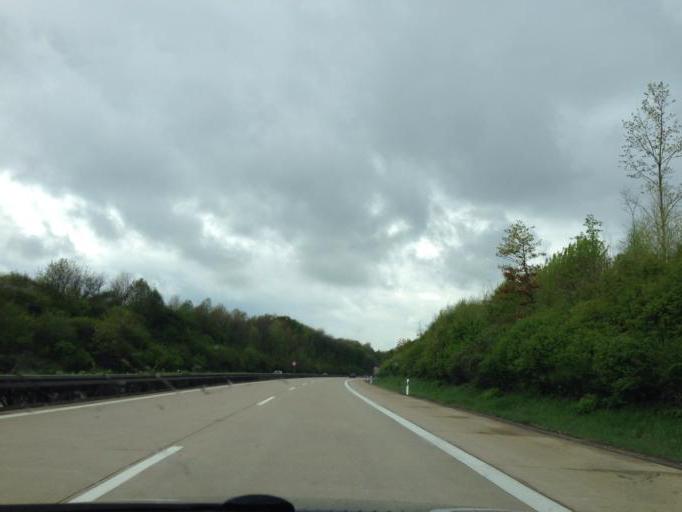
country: DE
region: Saxony
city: Nerchau
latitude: 51.2526
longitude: 12.7970
